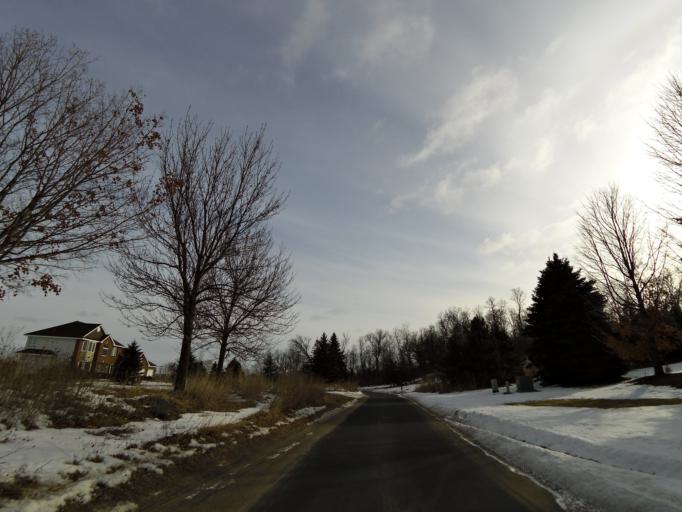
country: US
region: Wisconsin
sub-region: Saint Croix County
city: Hudson
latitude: 44.9813
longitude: -92.7931
